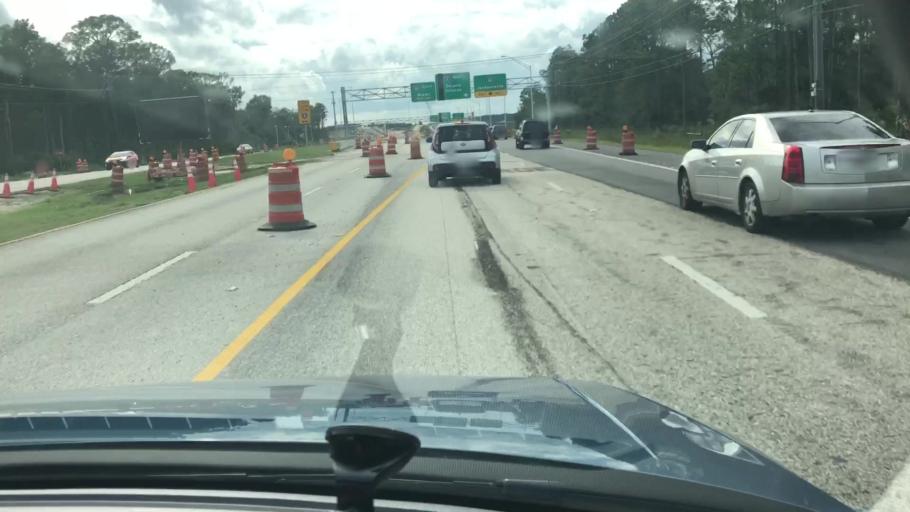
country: US
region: Florida
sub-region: Volusia County
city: South Daytona
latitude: 29.1586
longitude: -81.0685
